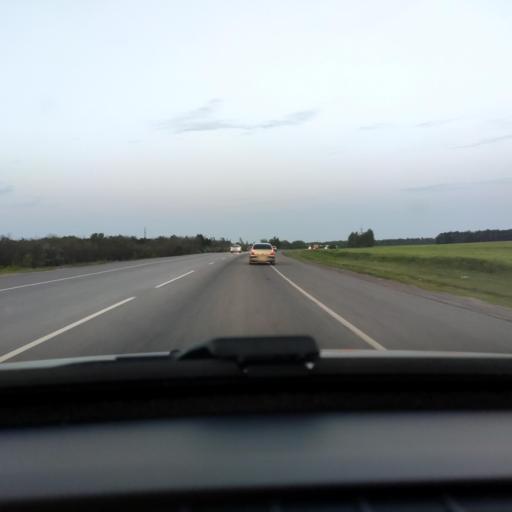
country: RU
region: Voronezj
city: Novaya Usman'
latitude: 51.7005
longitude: 39.4253
